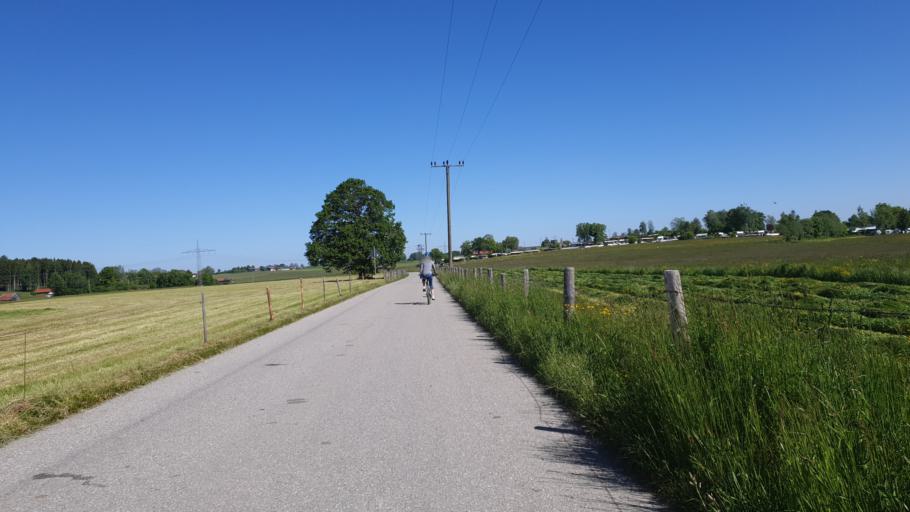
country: DE
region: Bavaria
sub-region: Upper Bavaria
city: Riegsee
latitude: 47.7017
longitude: 11.2157
